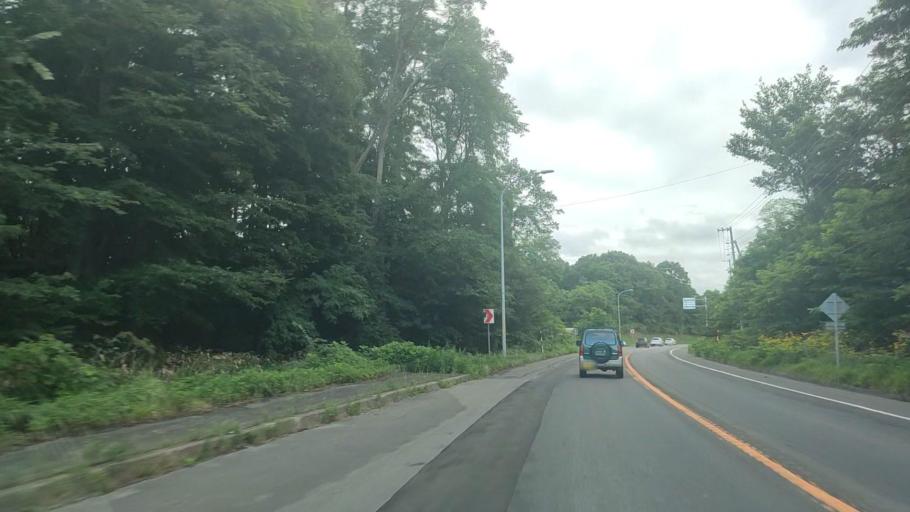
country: JP
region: Hokkaido
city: Nanae
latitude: 42.0656
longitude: 140.6029
